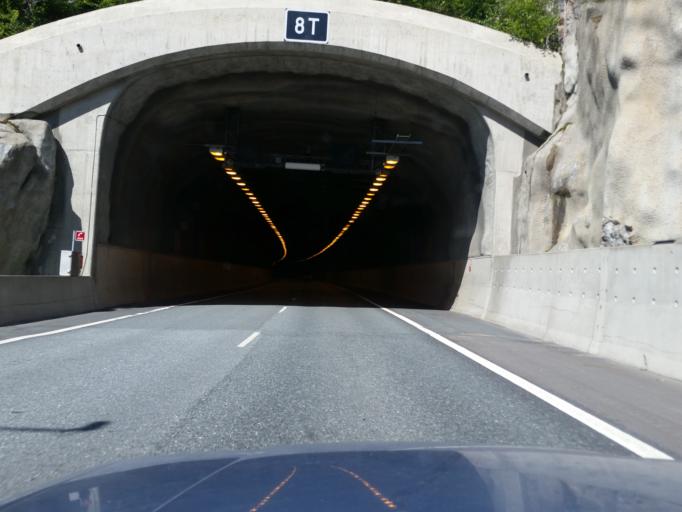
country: FI
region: Uusimaa
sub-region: Helsinki
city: Lohja
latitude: 60.3047
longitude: 24.0446
